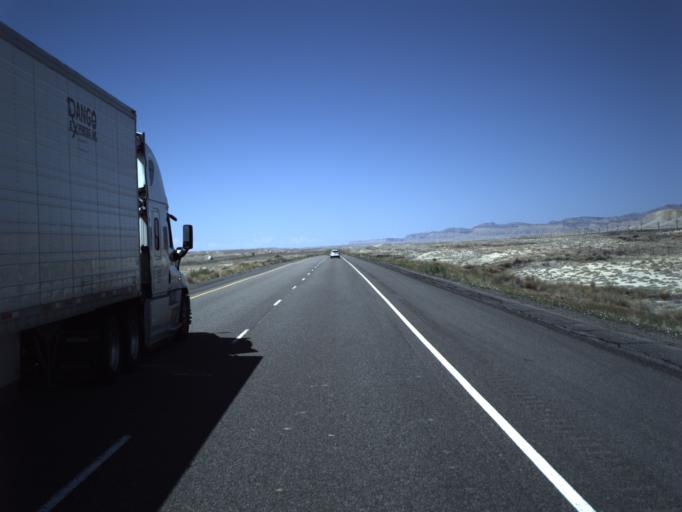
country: US
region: Utah
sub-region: Grand County
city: Moab
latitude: 38.9349
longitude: -109.4521
